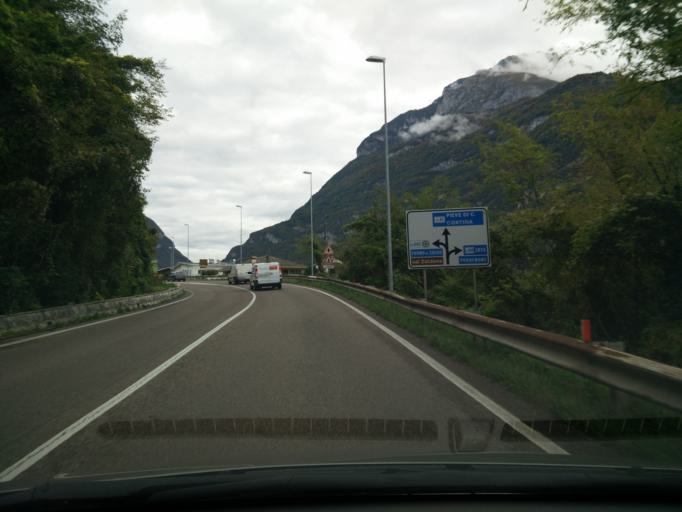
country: IT
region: Veneto
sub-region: Provincia di Belluno
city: Longarone
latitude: 46.2636
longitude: 12.3028
